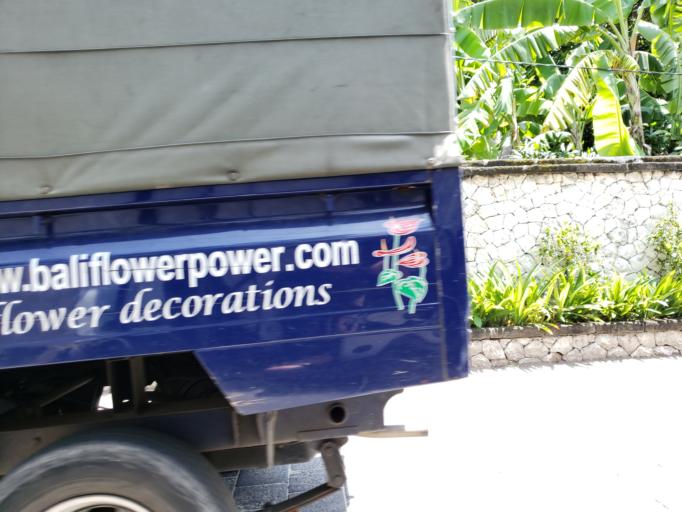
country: ID
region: Bali
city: Jimbaran
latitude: -8.7824
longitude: 115.1626
